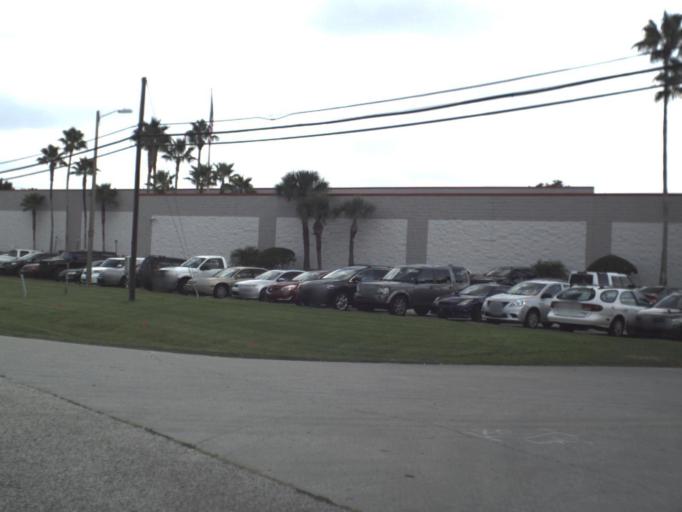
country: US
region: Florida
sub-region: Hillsborough County
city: Palm River-Clair Mel
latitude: 27.9498
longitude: -82.3602
